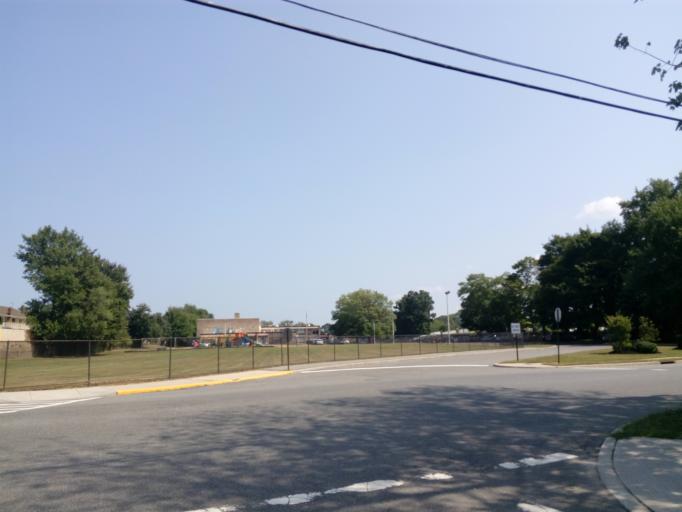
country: US
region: New York
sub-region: Nassau County
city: Glen Cove
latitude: 40.8761
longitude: -73.6226
